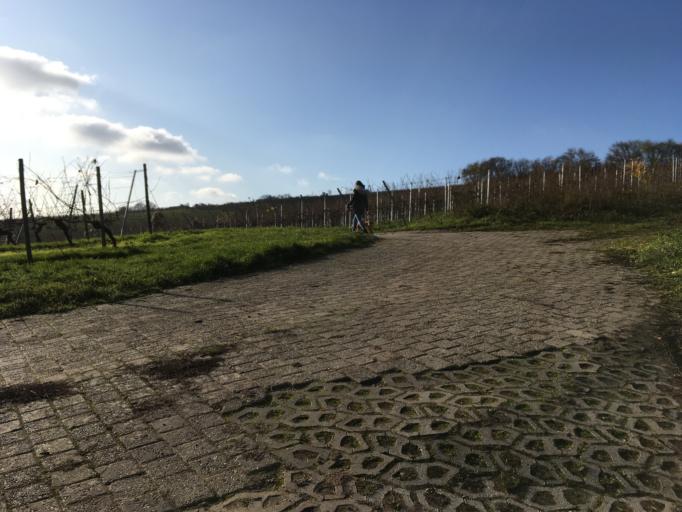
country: DE
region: Rheinland-Pfalz
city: Bodenheim
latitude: 49.9488
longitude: 8.3034
